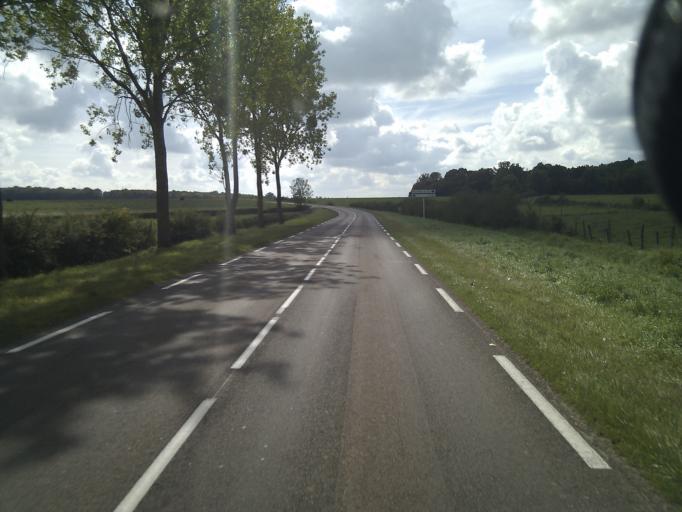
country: FR
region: Bourgogne
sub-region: Departement de la Cote-d'Or
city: Semur-en-Auxois
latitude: 47.4281
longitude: 4.3100
